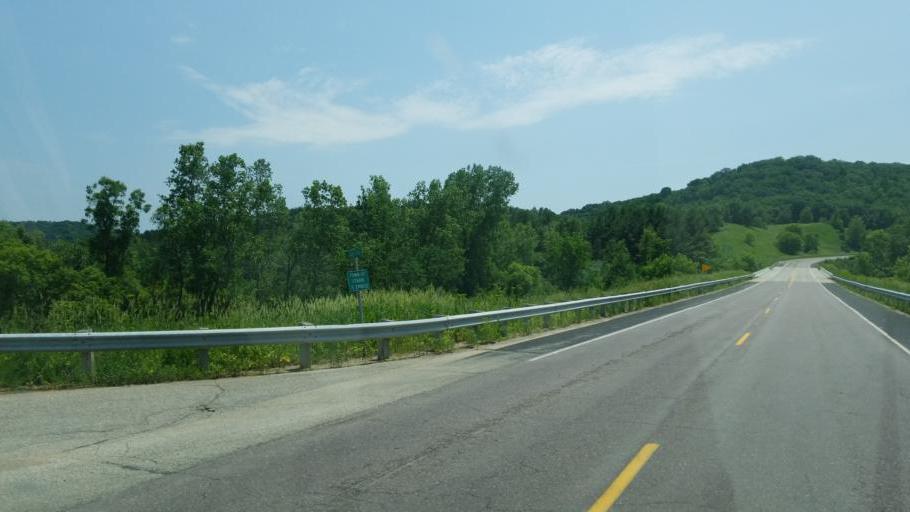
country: US
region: Wisconsin
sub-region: Monroe County
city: Cashton
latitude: 43.6313
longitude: -90.5989
